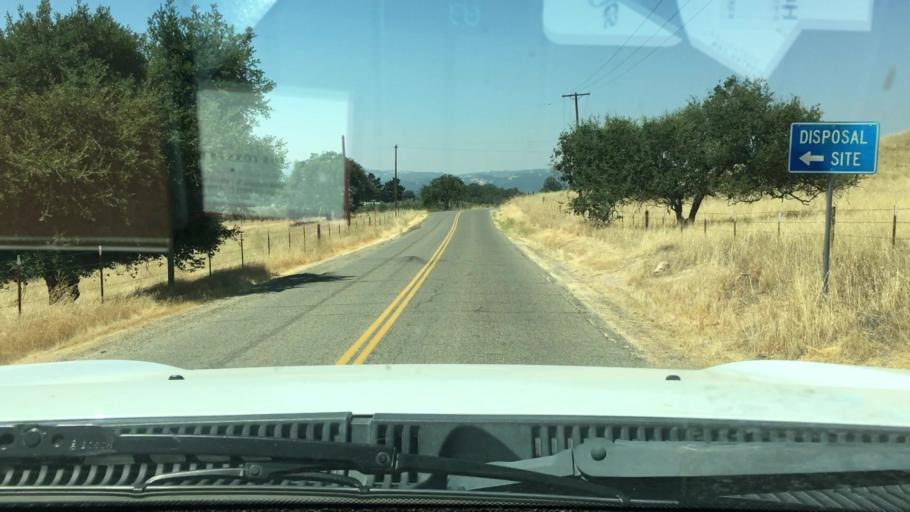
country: US
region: California
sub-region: San Luis Obispo County
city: Atascadero
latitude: 35.5252
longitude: -120.6407
